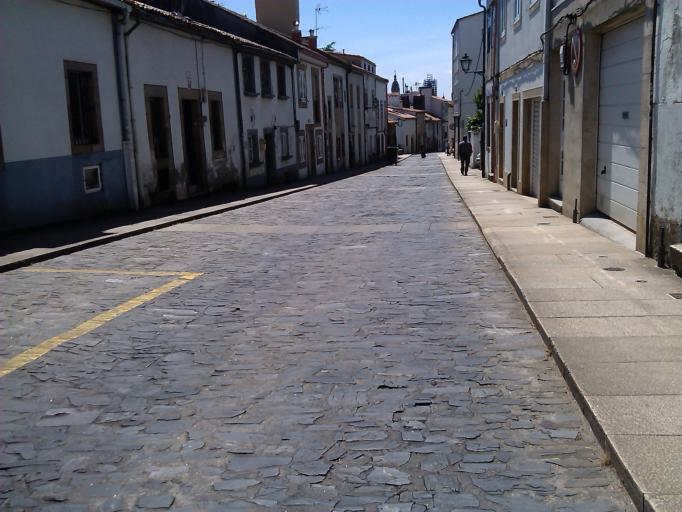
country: ES
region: Galicia
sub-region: Provincia da Coruna
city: Santiago de Compostela
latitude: 42.8821
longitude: -8.5366
